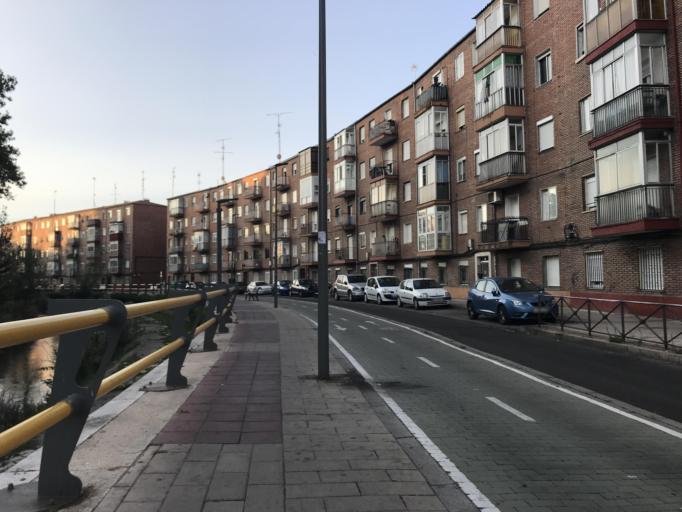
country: ES
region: Castille and Leon
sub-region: Provincia de Valladolid
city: Valladolid
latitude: 41.6522
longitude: -4.7119
